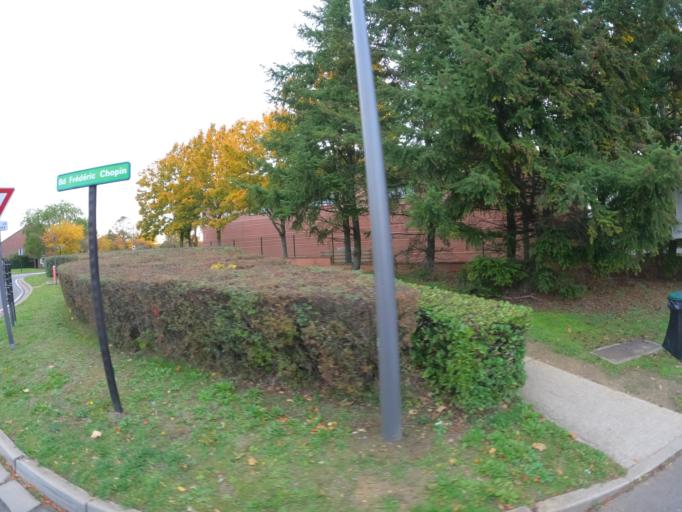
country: FR
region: Ile-de-France
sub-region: Departement de Seine-et-Marne
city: Lognes
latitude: 48.8367
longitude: 2.6426
